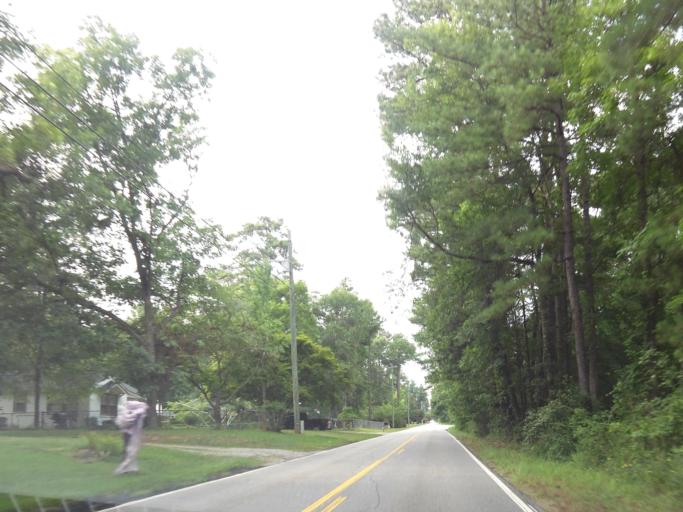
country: US
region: Georgia
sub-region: Bibb County
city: West Point
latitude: 32.9008
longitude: -83.7745
